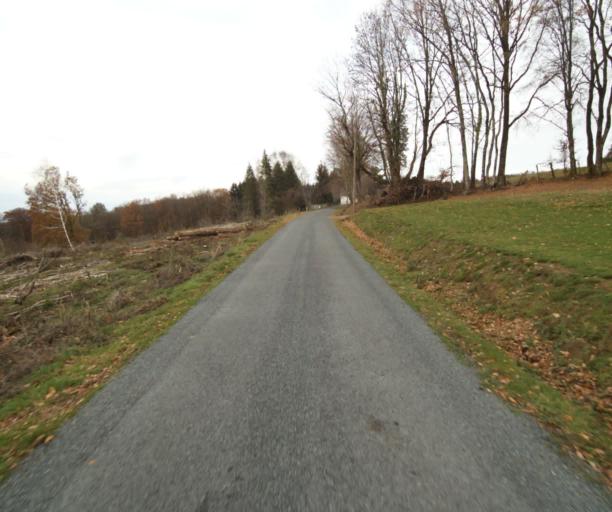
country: FR
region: Limousin
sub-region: Departement de la Correze
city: Saint-Mexant
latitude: 45.2532
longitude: 1.6561
